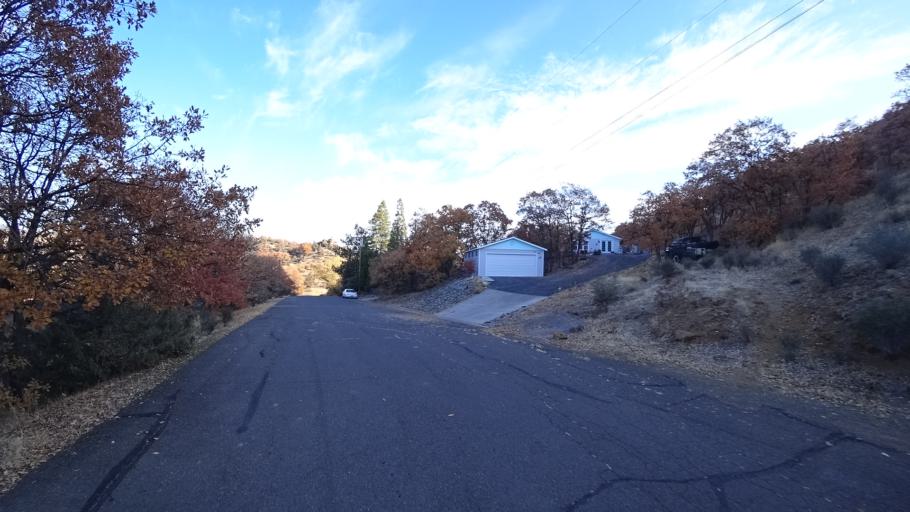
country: US
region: California
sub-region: Siskiyou County
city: Yreka
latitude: 41.7099
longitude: -122.6158
